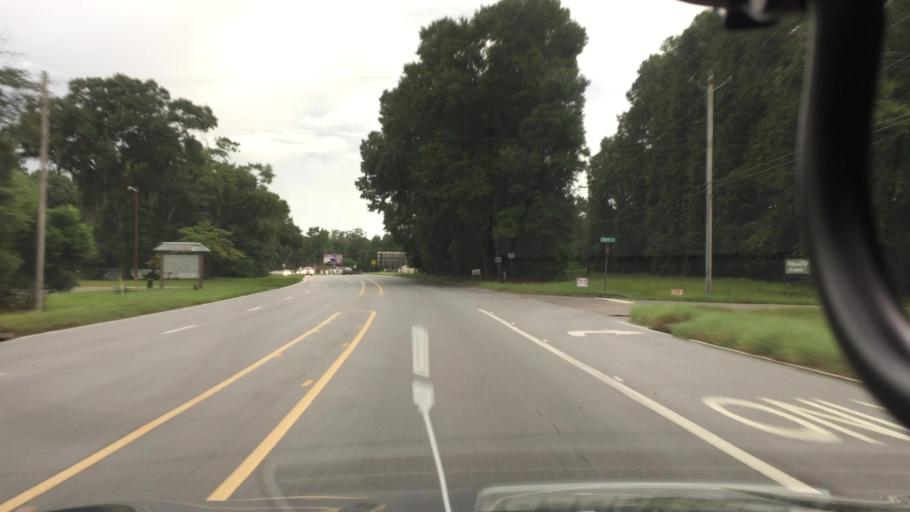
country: US
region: Alabama
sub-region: Pike County
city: Troy
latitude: 31.7583
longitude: -85.9613
